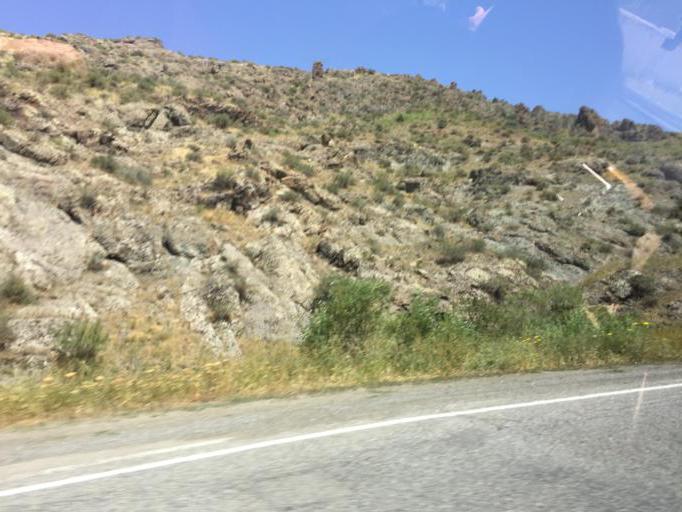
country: AM
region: Vayots' Dzori Marz
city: Jermuk
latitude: 39.7166
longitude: 45.6255
